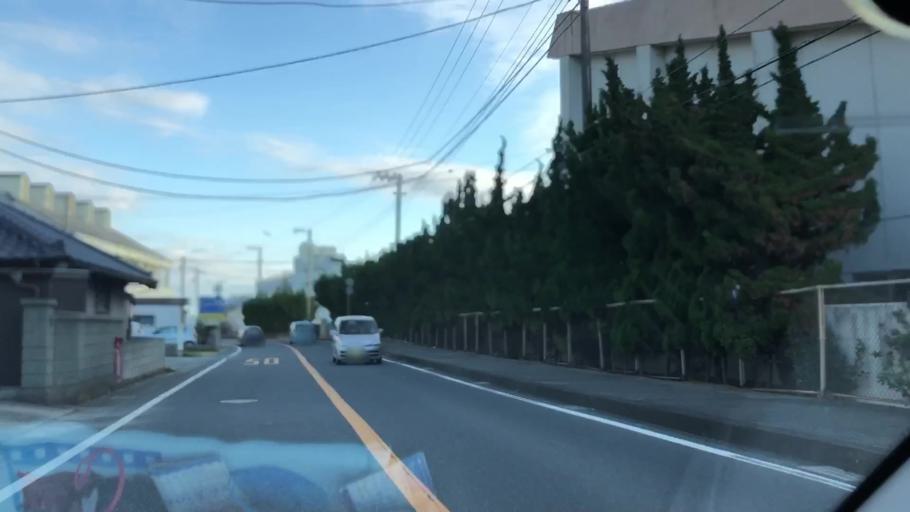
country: JP
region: Chiba
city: Tateyama
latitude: 34.9371
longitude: 139.9576
